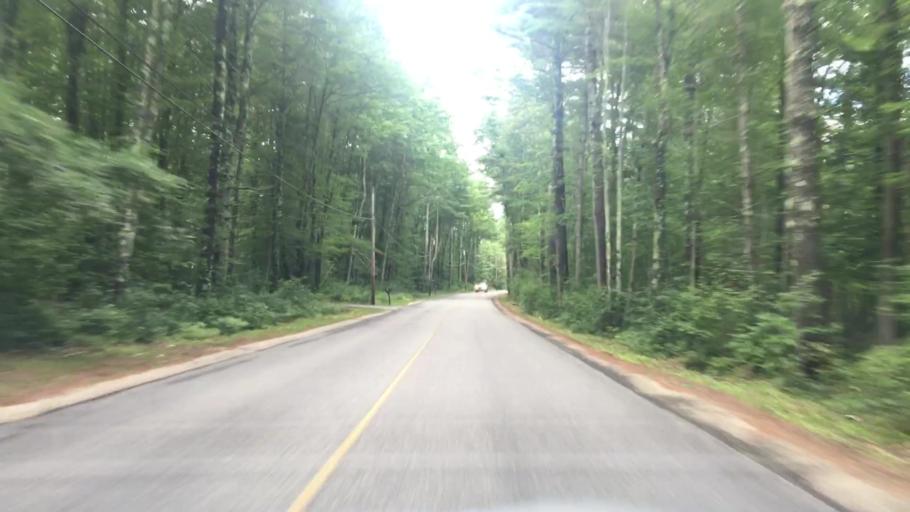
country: US
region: Maine
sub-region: York County
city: Dayton
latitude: 43.5310
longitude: -70.5851
